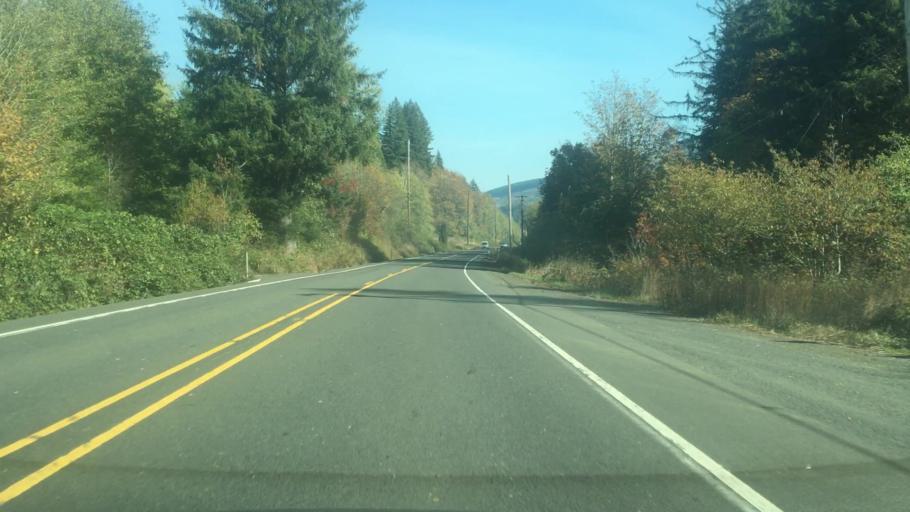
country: US
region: Oregon
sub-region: Lincoln County
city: Rose Lodge
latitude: 45.0215
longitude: -123.8474
